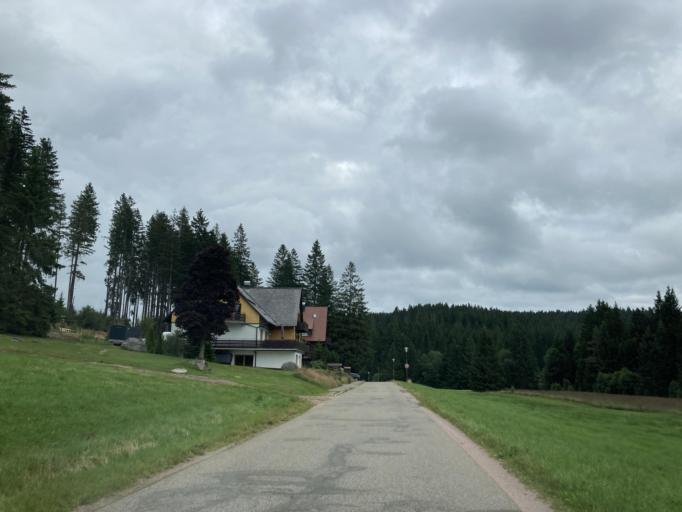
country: DE
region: Baden-Wuerttemberg
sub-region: Freiburg Region
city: Schonwald im Schwarzwald
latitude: 48.1181
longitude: 8.2087
